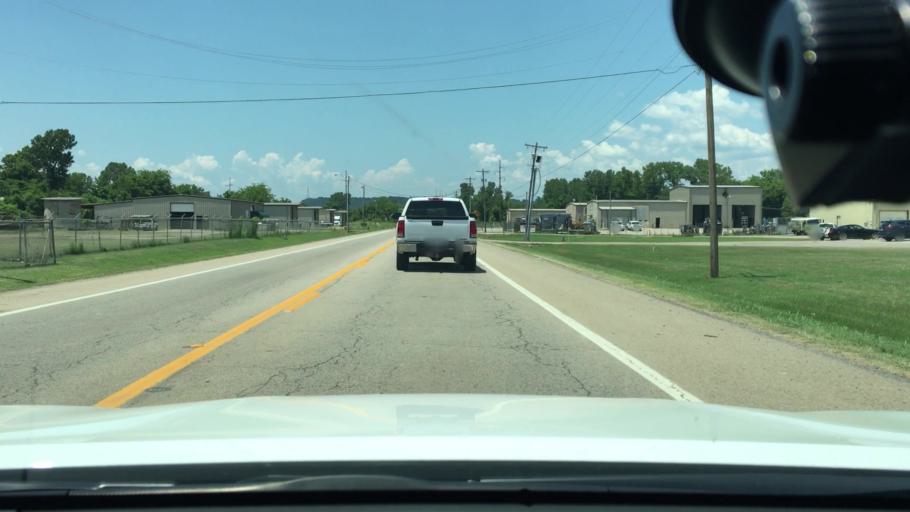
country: US
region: Arkansas
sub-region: Crawford County
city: Van Buren
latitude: 35.4162
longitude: -94.3326
